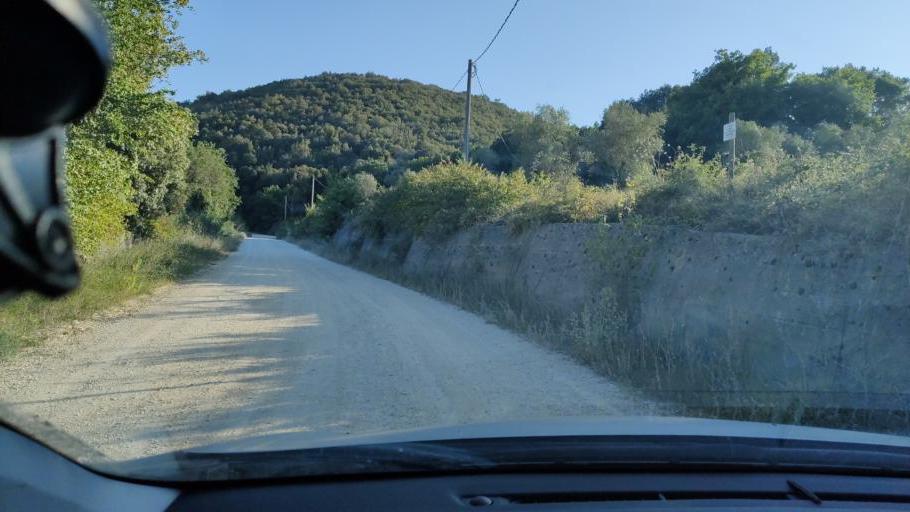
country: IT
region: Umbria
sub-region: Provincia di Terni
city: Amelia
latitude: 42.5428
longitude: 12.3824
